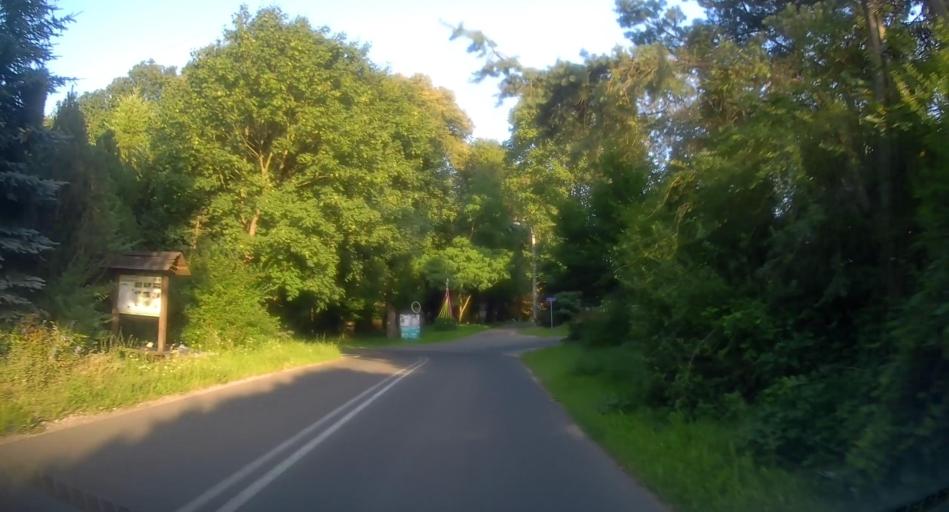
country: PL
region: Lodz Voivodeship
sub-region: Powiat skierniewicki
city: Kowiesy
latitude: 51.8915
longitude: 20.3877
